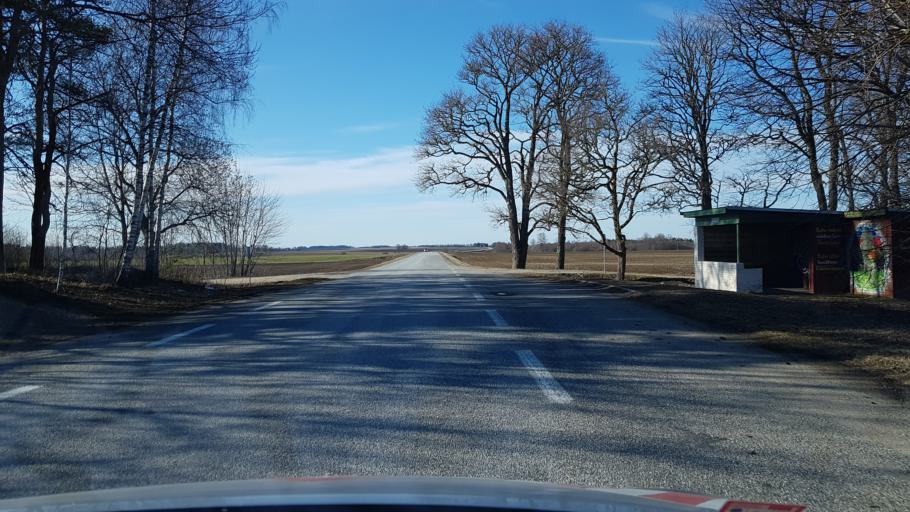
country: EE
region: Laeaene-Virumaa
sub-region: Kadrina vald
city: Kadrina
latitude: 59.3106
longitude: 26.1572
